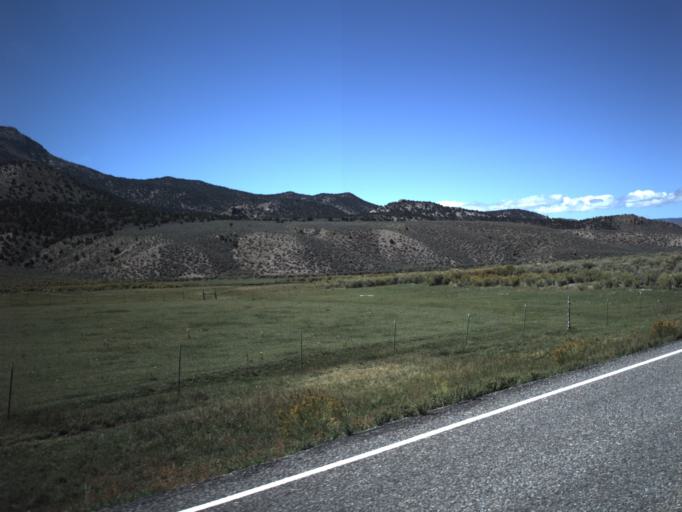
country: US
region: Utah
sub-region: Piute County
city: Junction
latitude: 38.1717
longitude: -112.0599
